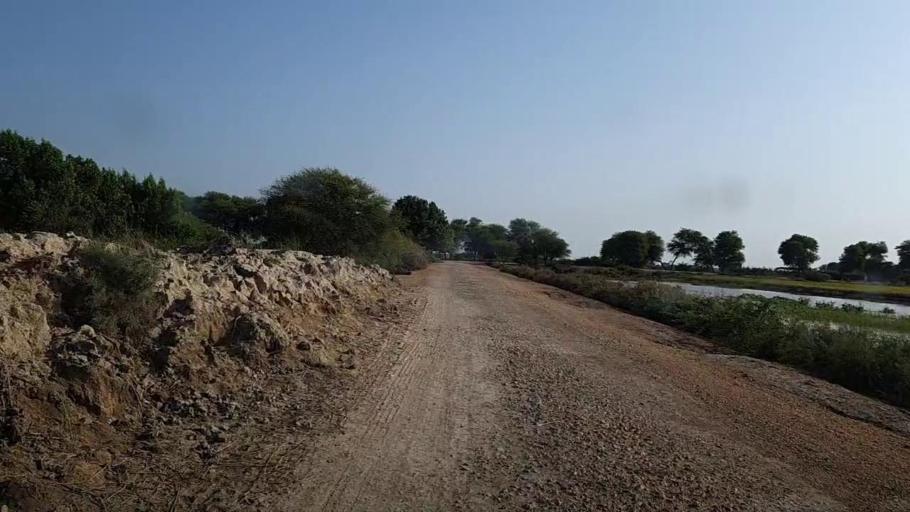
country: PK
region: Sindh
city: Bulri
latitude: 24.7707
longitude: 68.4356
